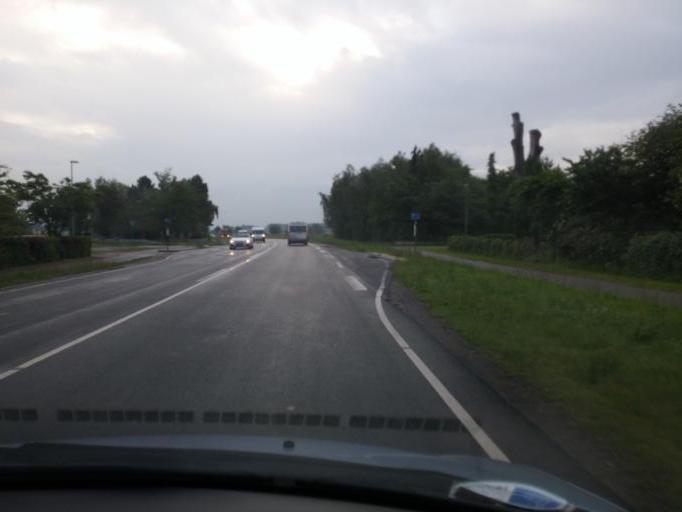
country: DK
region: South Denmark
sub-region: Kerteminde Kommune
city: Munkebo
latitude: 55.4405
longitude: 10.5166
